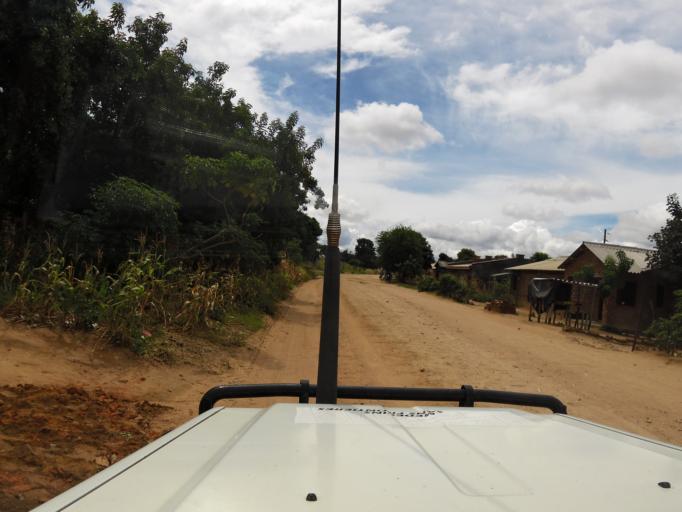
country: ZW
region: Harare
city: Epworth
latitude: -17.8957
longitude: 31.1399
